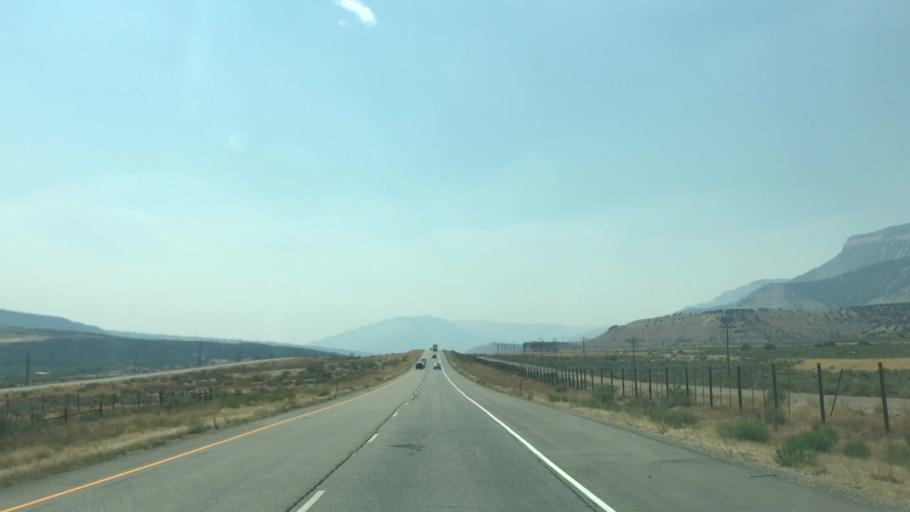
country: US
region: Colorado
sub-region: Garfield County
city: Rifle
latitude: 39.5038
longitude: -107.9006
